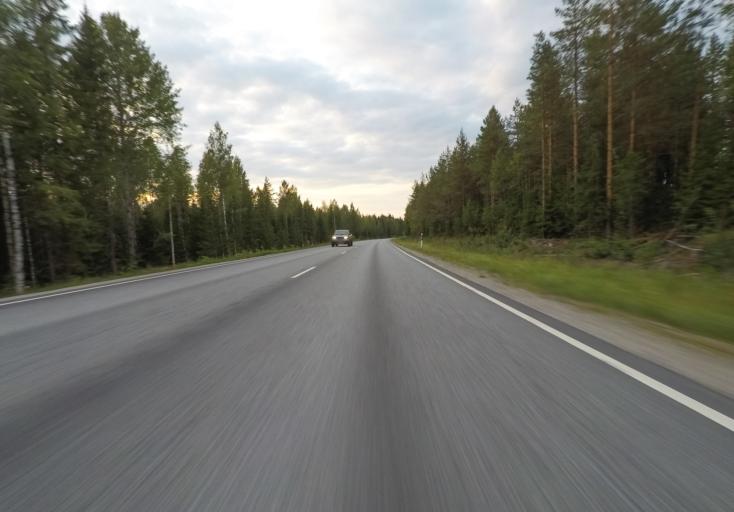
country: FI
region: Central Finland
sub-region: Jyvaeskylae
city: Toivakka
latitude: 62.2405
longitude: 26.1789
